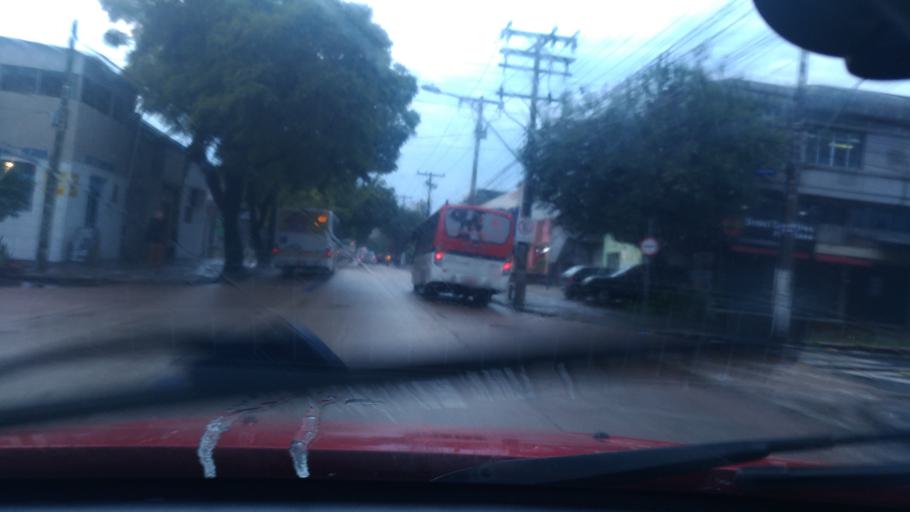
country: BR
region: Rio Grande do Sul
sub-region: Porto Alegre
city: Porto Alegre
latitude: -30.0063
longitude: -51.1974
